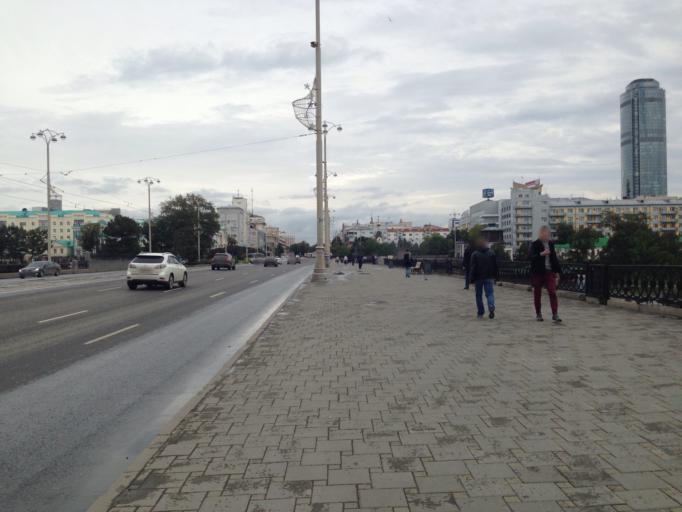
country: RU
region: Sverdlovsk
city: Yekaterinburg
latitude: 56.8380
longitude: 60.6020
